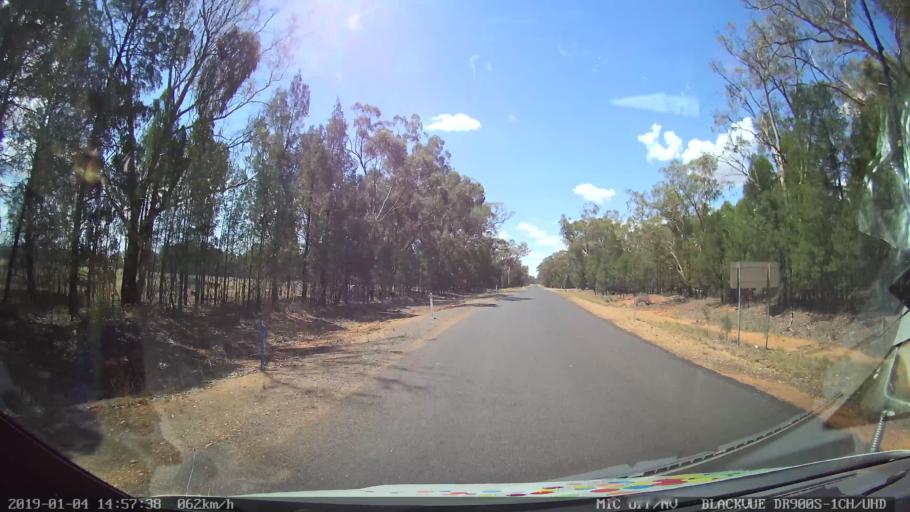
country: AU
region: New South Wales
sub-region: Gilgandra
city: Gilgandra
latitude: -31.9641
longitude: 148.6306
